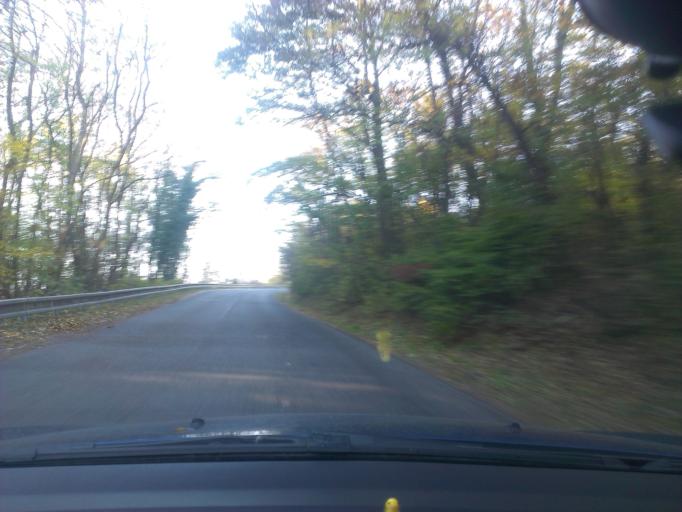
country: SK
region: Trnavsky
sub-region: Okres Trnava
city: Piestany
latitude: 48.5646
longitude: 17.8659
